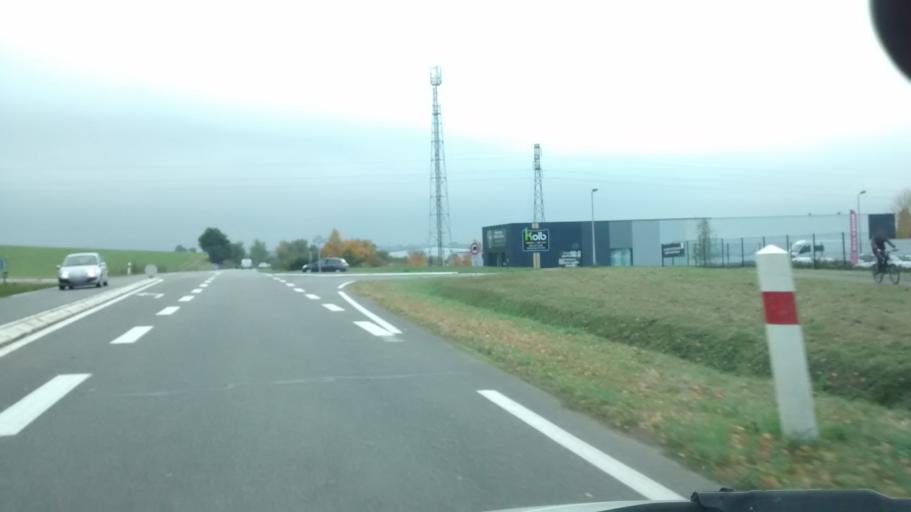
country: FR
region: Brittany
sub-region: Departement d'Ille-et-Vilaine
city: Acigne
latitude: 48.1393
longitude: -1.5163
